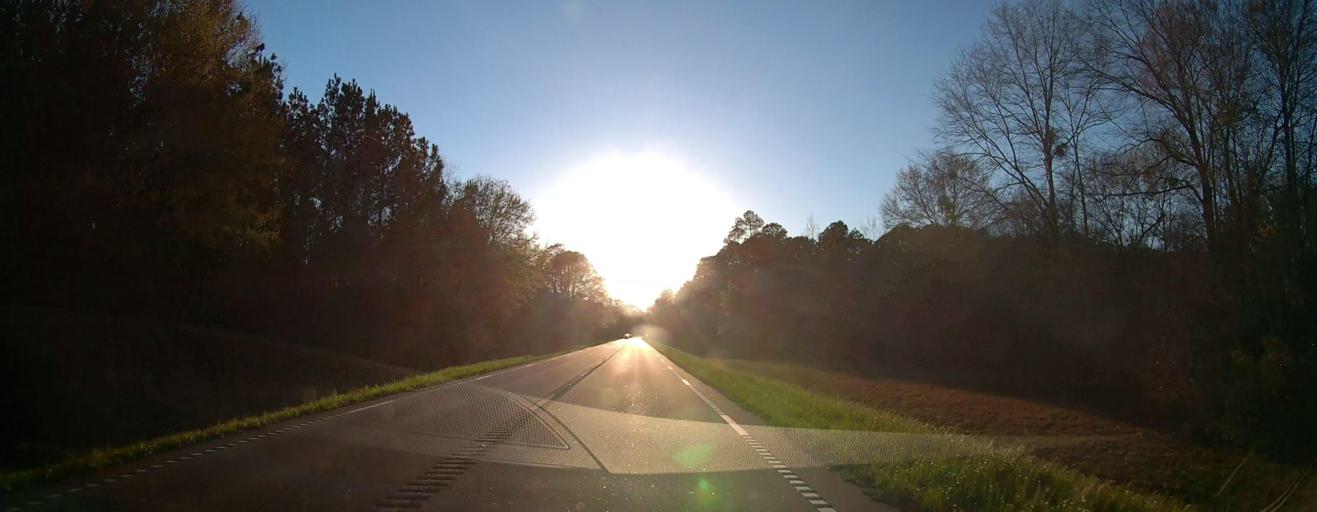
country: US
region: Georgia
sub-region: Wilcox County
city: Rochelle
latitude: 31.9574
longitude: -83.6183
